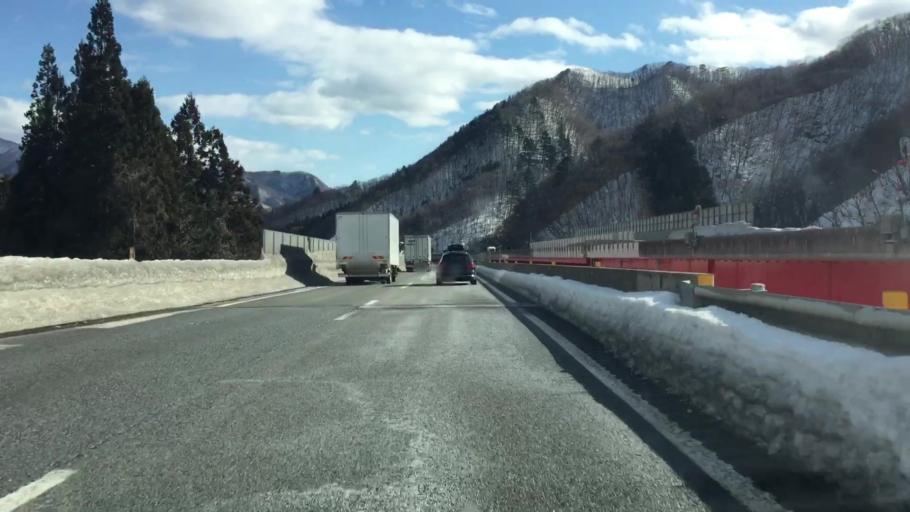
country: JP
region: Gunma
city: Numata
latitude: 36.7768
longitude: 138.9457
